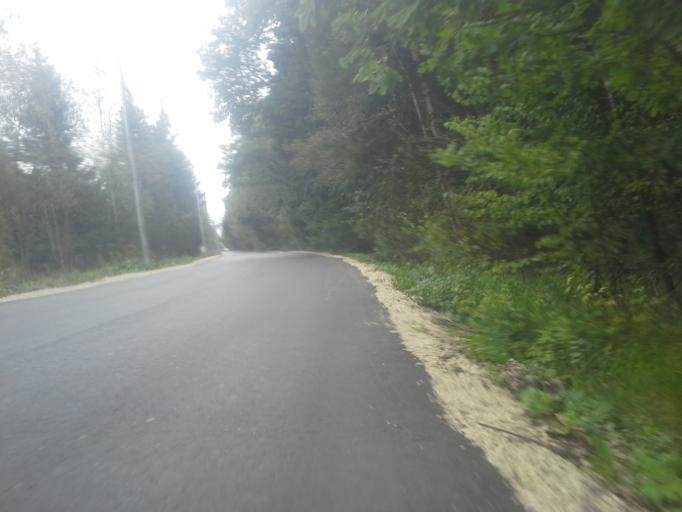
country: RU
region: Moskovskaya
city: Kievskij
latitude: 55.4425
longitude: 36.8984
